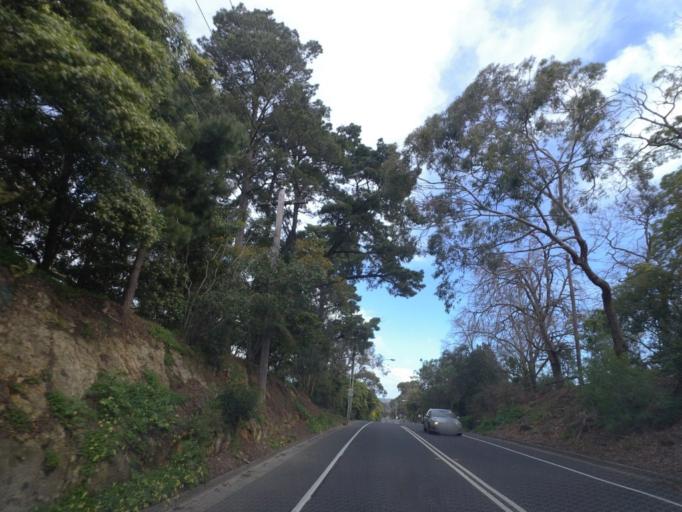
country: AU
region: Victoria
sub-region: Whitehorse
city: Vermont
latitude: -37.8432
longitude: 145.1900
